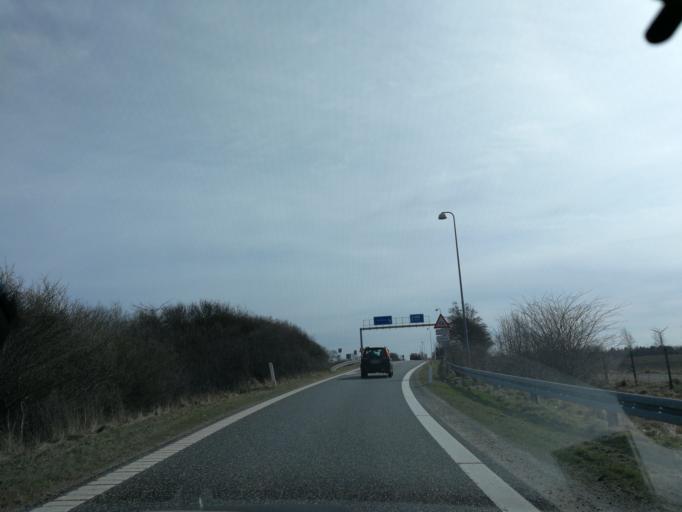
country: DK
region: North Denmark
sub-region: Alborg Kommune
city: Vodskov
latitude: 57.0966
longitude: 10.0177
